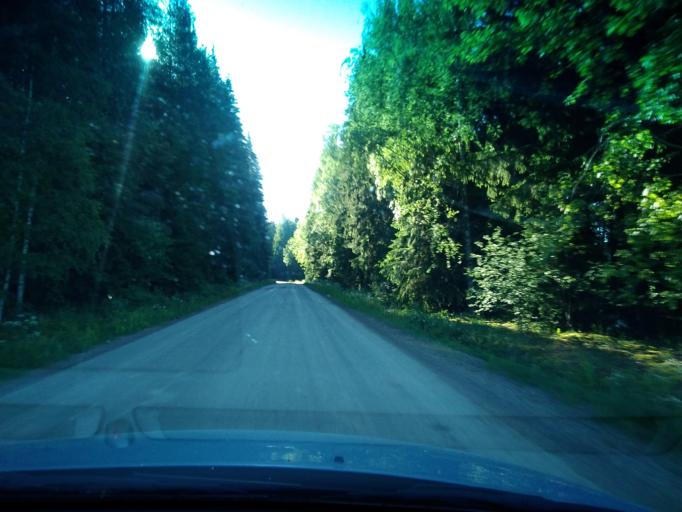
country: FI
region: Haeme
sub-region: Forssa
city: Tammela
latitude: 60.7613
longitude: 23.7928
